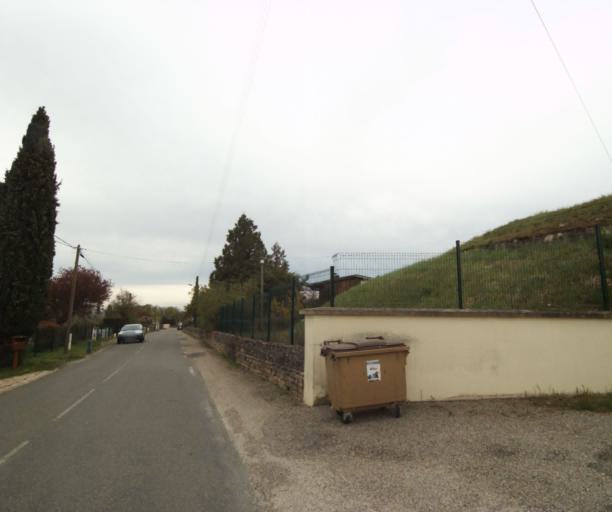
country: FR
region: Bourgogne
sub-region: Departement de Saone-et-Loire
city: Charnay-les-Macon
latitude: 46.3210
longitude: 4.7866
